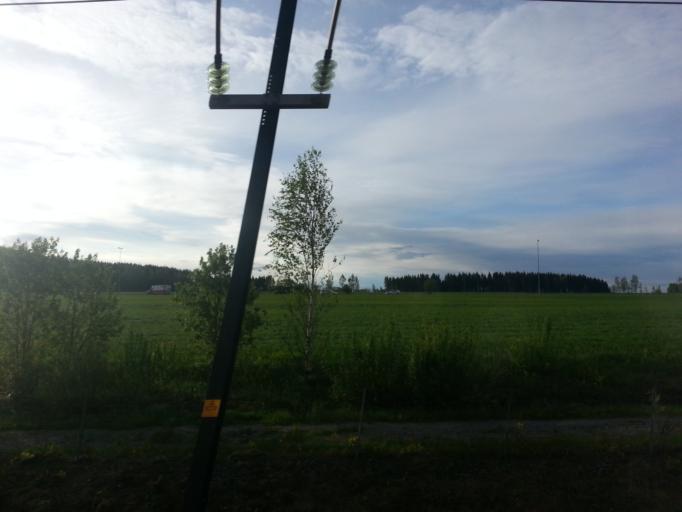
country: NO
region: Akershus
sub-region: Ullensaker
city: Jessheim
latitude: 60.1174
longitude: 11.1556
